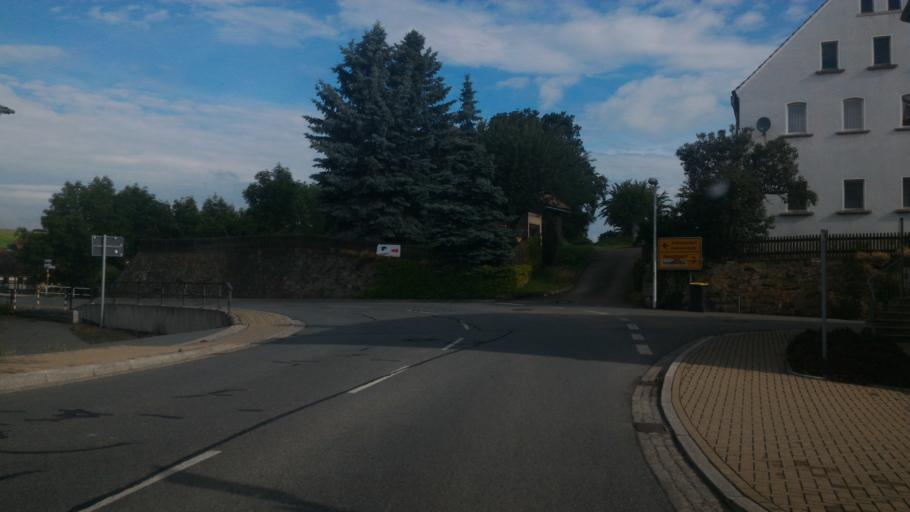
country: DE
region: Saxony
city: Mittelherwigsdorf
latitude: 50.9148
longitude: 14.7510
